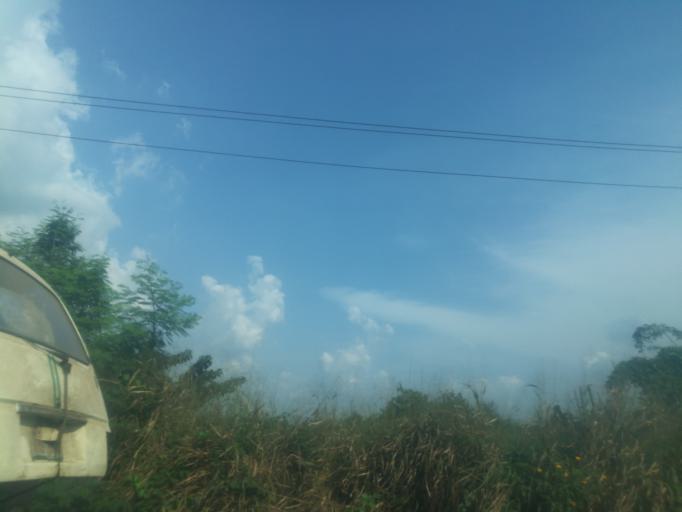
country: NG
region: Ogun
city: Abeokuta
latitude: 7.1076
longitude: 3.2974
